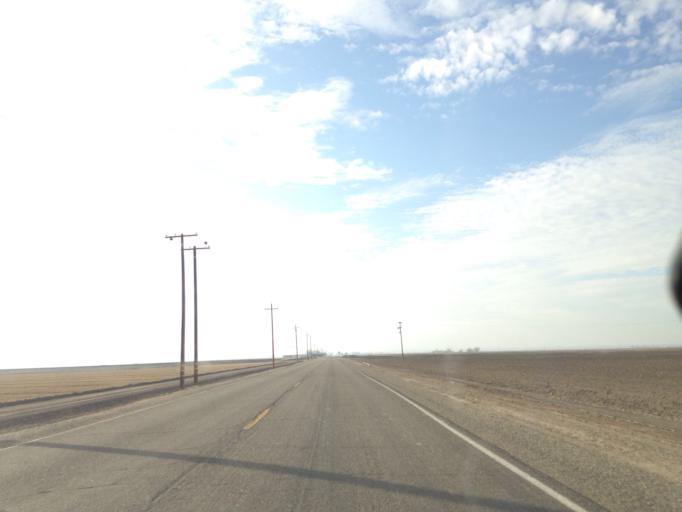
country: US
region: California
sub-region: Kern County
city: Buttonwillow
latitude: 35.4417
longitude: -119.5462
